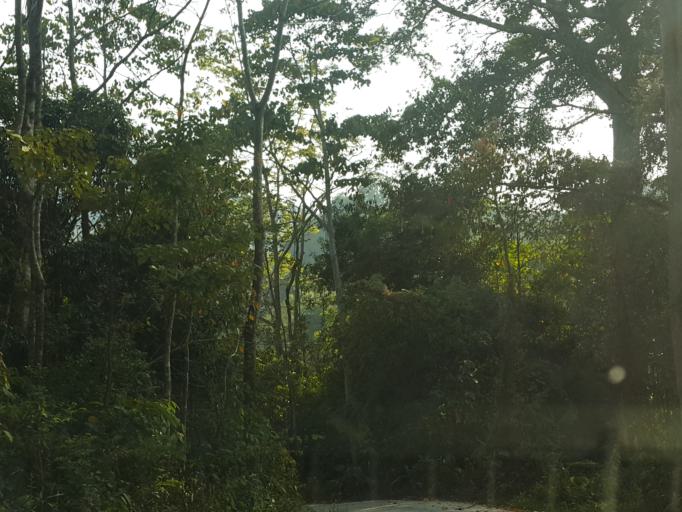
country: TH
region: Chiang Mai
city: Samoeng
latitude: 19.0183
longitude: 98.7603
